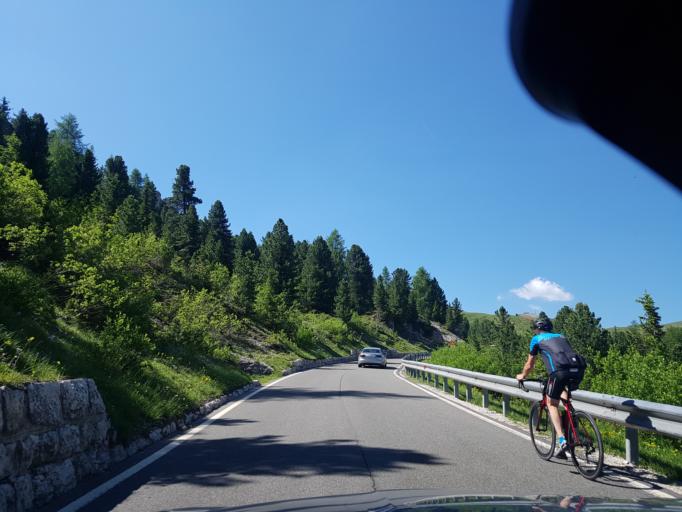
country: IT
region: Trentino-Alto Adige
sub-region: Bolzano
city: Selva
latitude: 46.5180
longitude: 11.7697
